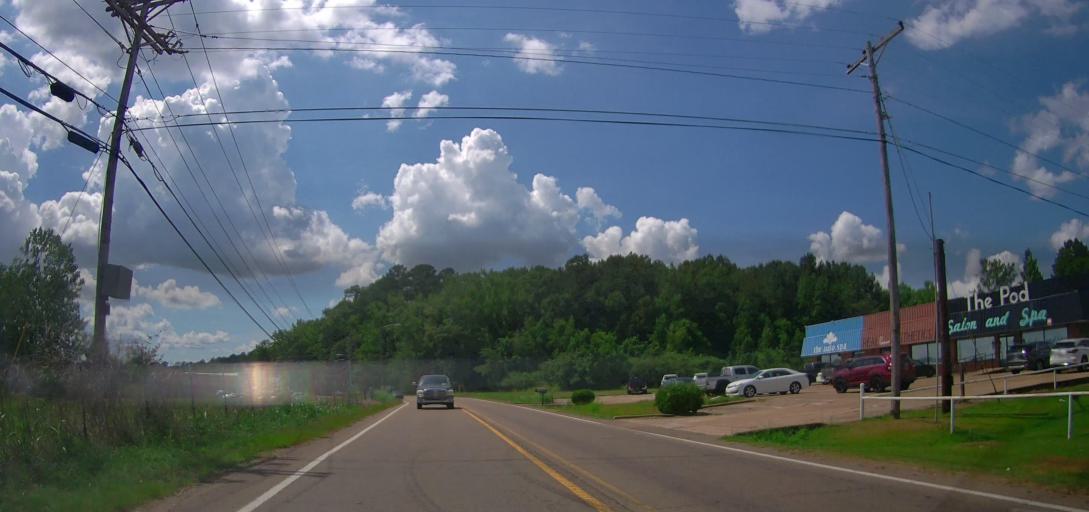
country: US
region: Mississippi
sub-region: Lowndes County
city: Columbus
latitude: 33.5374
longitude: -88.4325
